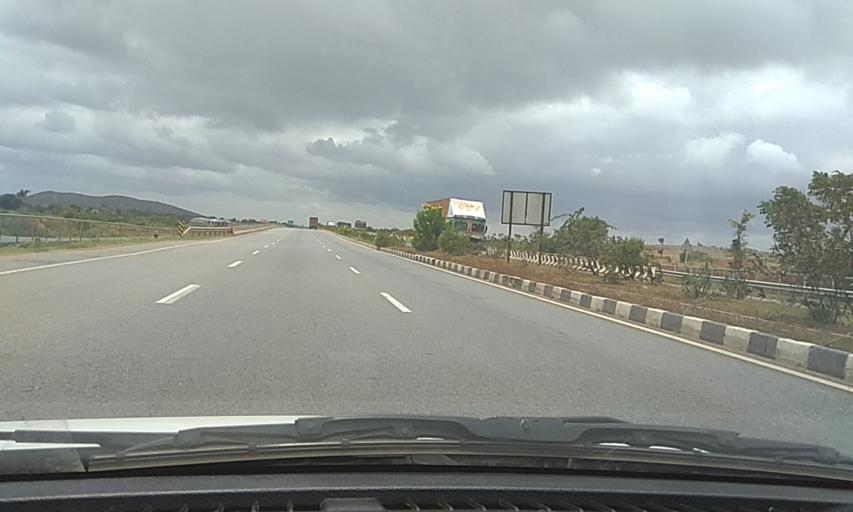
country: IN
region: Karnataka
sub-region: Chitradurga
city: Chitradurga
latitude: 14.1716
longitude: 76.4698
